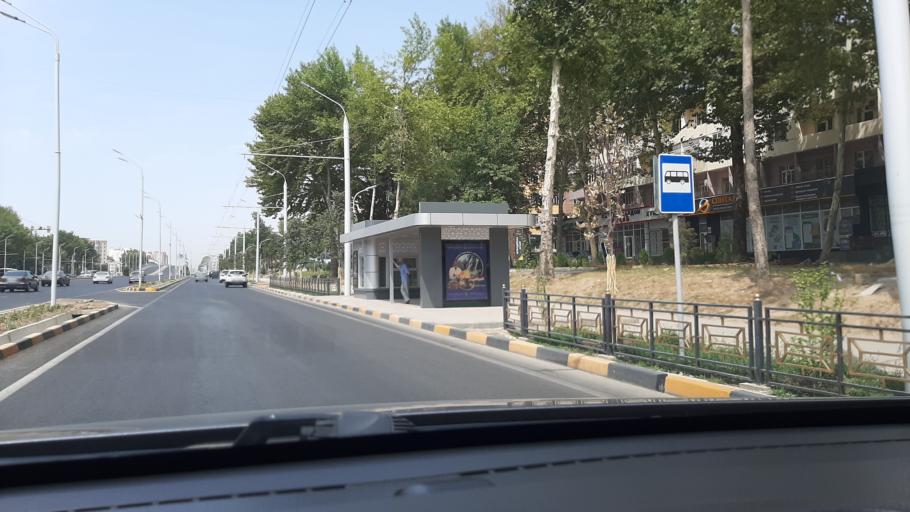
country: TJ
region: Dushanbe
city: Dushanbe
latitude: 38.5842
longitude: 68.7485
